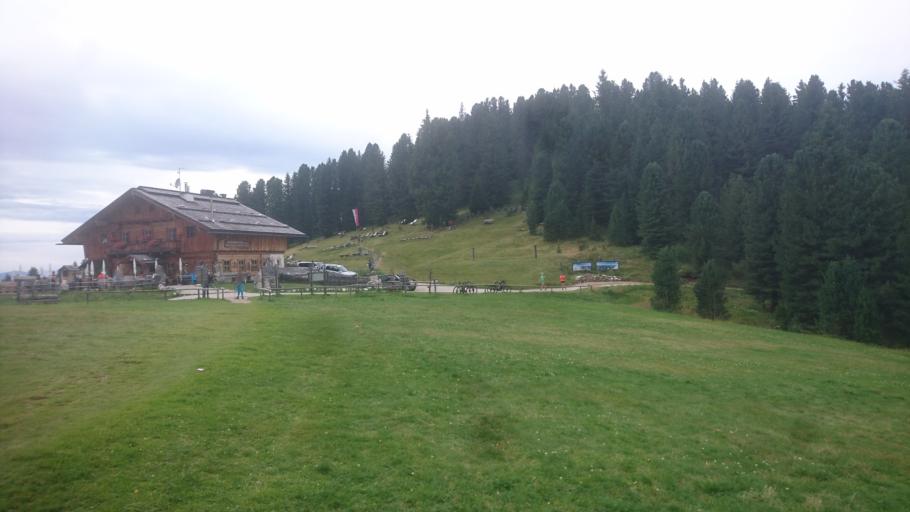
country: IT
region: Trentino-Alto Adige
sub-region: Bolzano
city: Santa Cristina Valgardena
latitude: 46.6207
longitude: 11.7503
